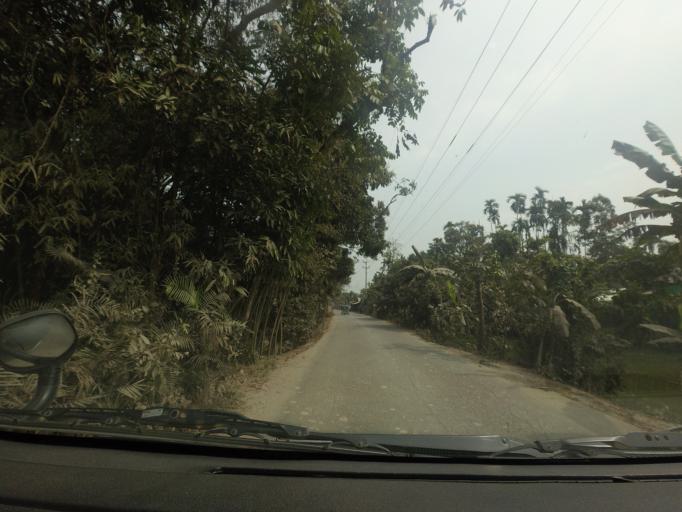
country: BD
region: Dhaka
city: Kishorganj
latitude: 24.3435
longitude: 90.7767
